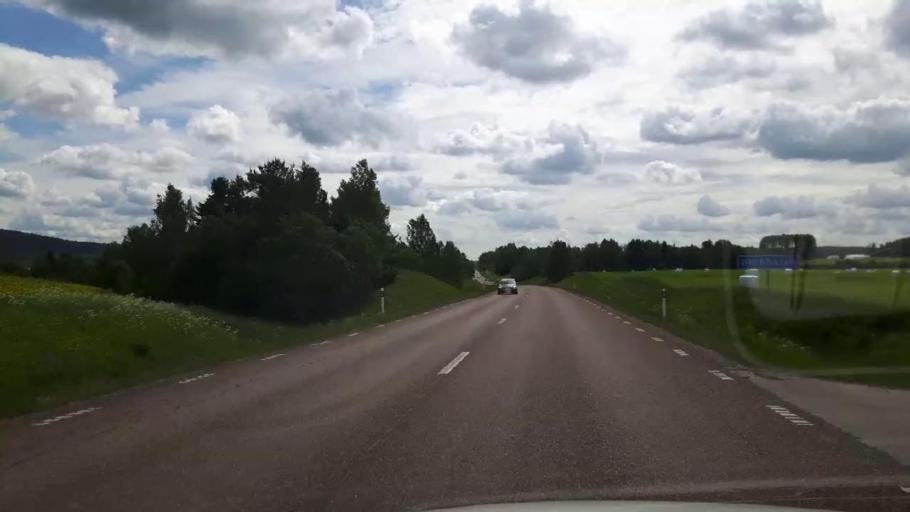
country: SE
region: Dalarna
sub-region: Hedemora Kommun
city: Langshyttan
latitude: 60.3855
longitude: 15.9053
